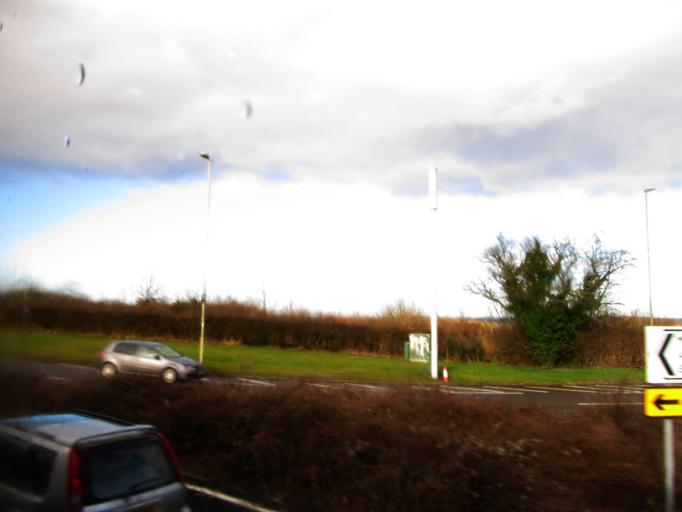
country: GB
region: England
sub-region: Hampshire
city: Basingstoke
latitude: 51.2352
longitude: -1.1413
